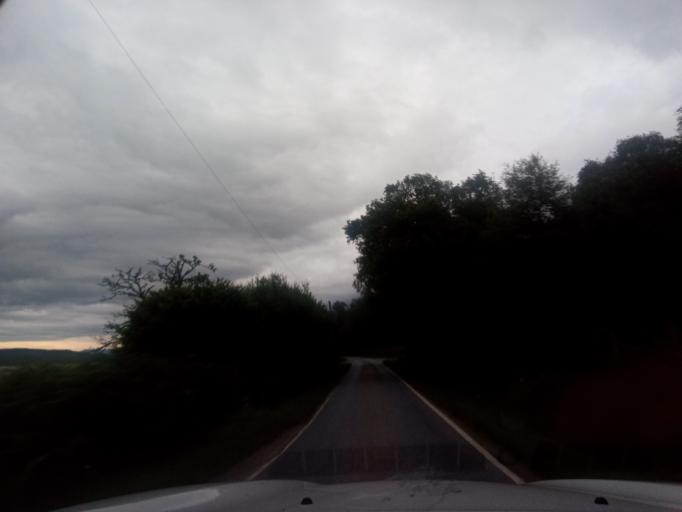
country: GB
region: Scotland
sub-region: Highland
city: Fort William
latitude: 56.8460
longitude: -5.2831
